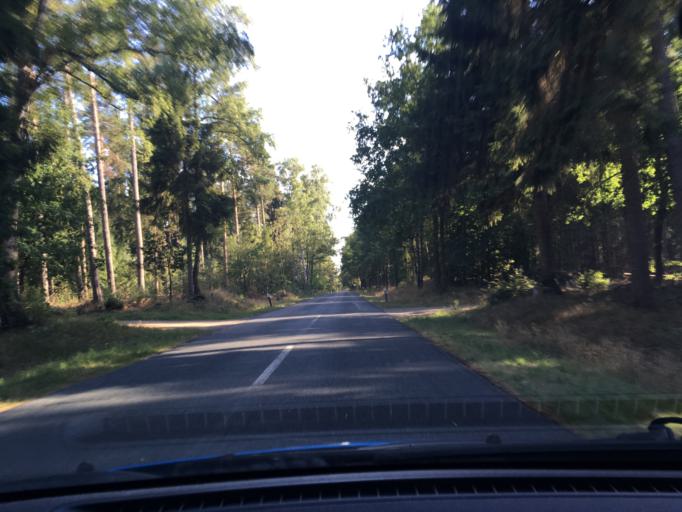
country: DE
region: Lower Saxony
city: Thomasburg
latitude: 53.2429
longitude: 10.7062
